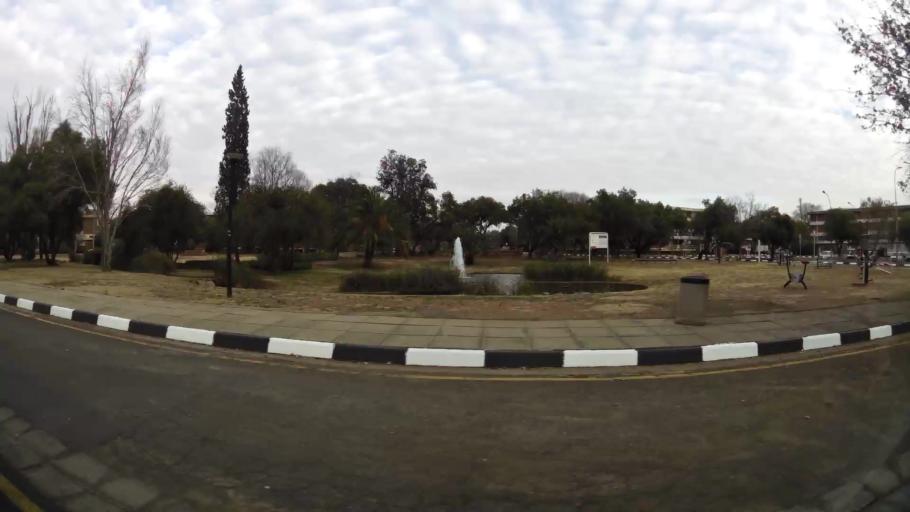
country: ZA
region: Orange Free State
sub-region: Mangaung Metropolitan Municipality
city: Bloemfontein
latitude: -29.1082
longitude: 26.1921
